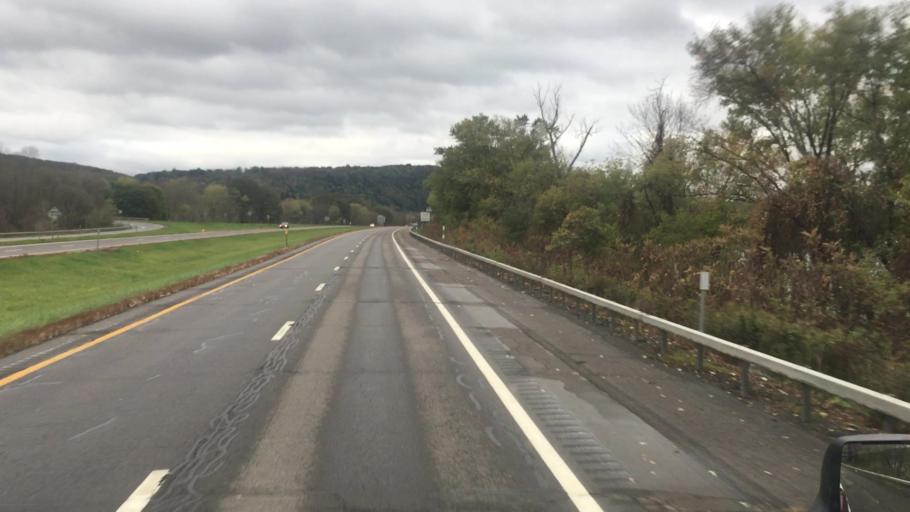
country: US
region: New York
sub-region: Tioga County
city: Owego
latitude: 42.0970
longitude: -76.2624
